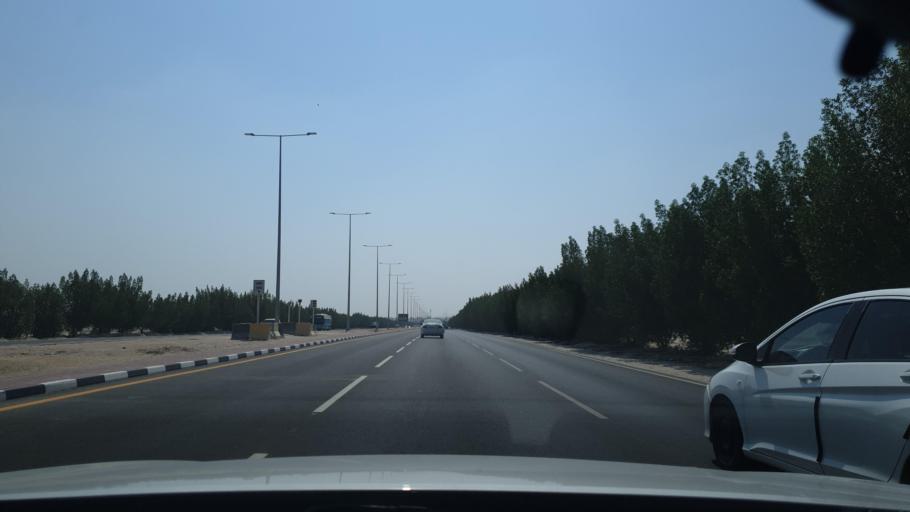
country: QA
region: Al Khawr
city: Al Khawr
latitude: 25.7036
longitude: 51.5035
